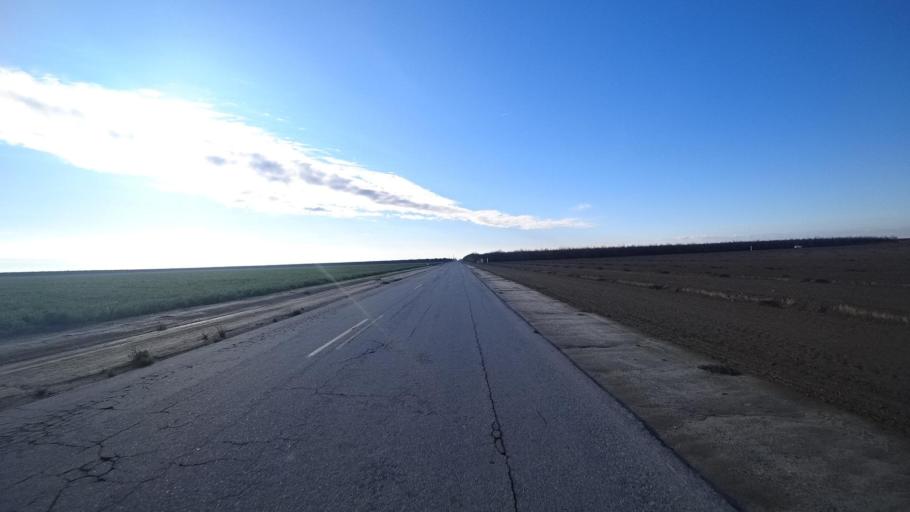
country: US
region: California
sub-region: Kern County
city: Delano
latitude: 35.7486
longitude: -119.3300
